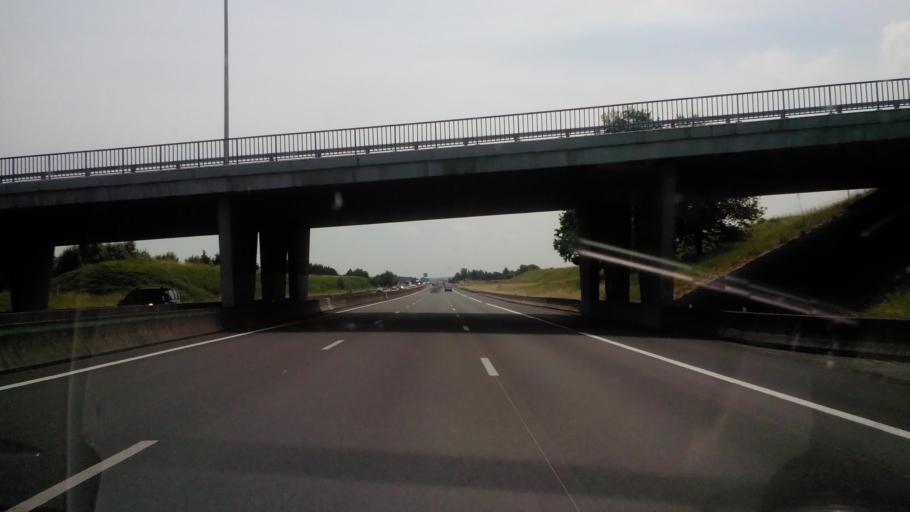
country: FR
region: Bourgogne
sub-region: Departement de Saone-et-Loire
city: Charnay-les-Macon
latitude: 46.3103
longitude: 4.7936
